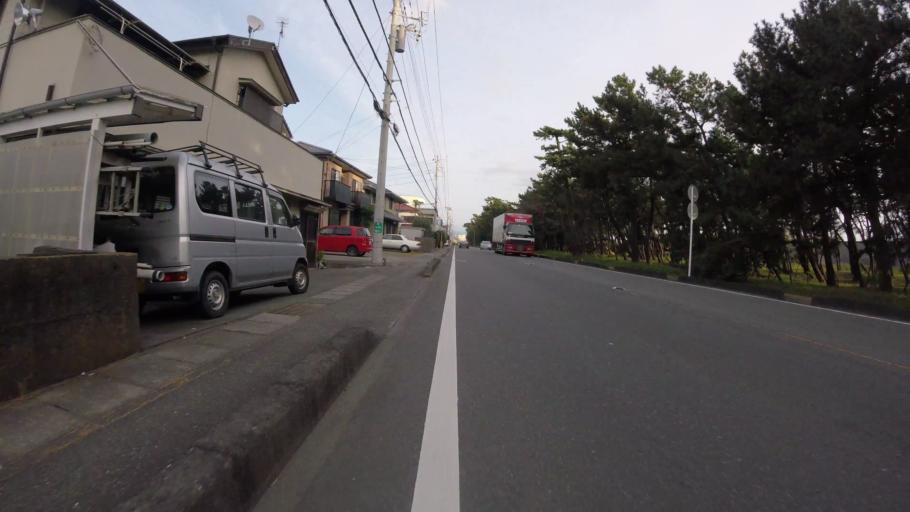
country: JP
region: Shizuoka
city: Numazu
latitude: 35.1249
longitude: 138.7890
